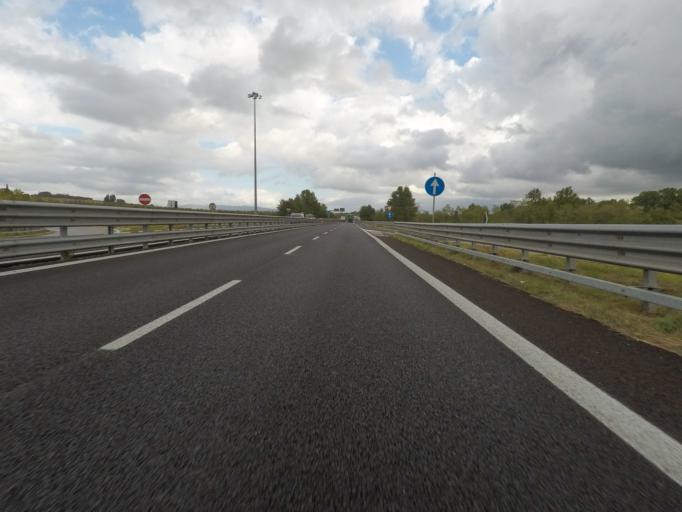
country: IT
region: Tuscany
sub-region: Provincia di Siena
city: Arbia
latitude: 43.2997
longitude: 11.4040
